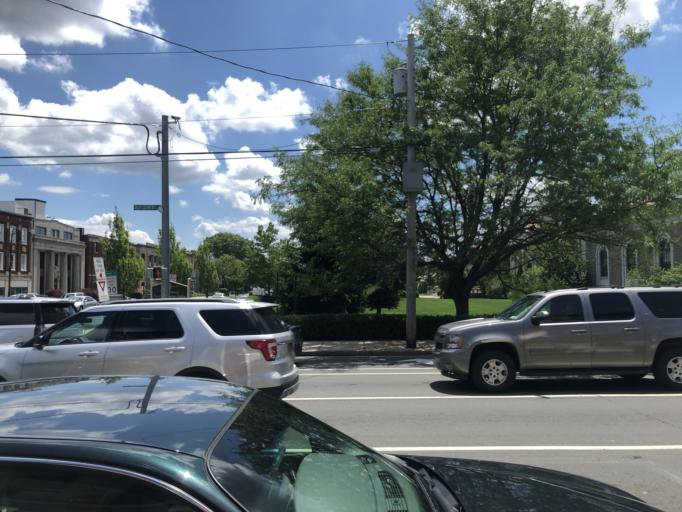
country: US
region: New York
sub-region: Nassau County
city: Mineola
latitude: 40.7390
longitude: -73.6395
